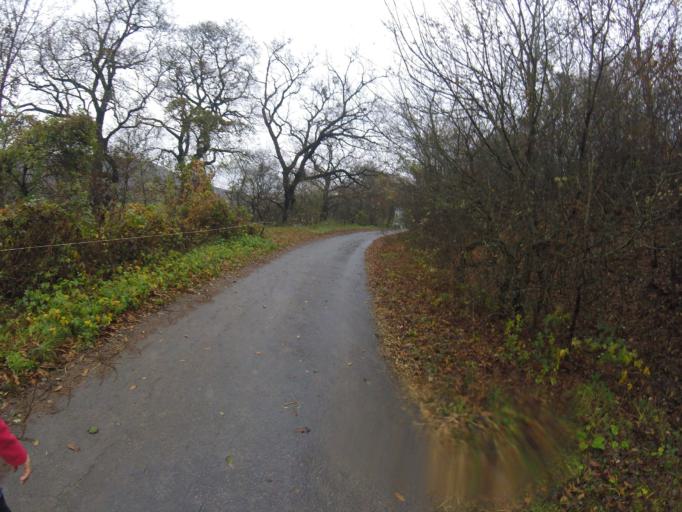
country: HU
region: Nograd
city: Rimoc
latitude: 47.9997
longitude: 19.5813
